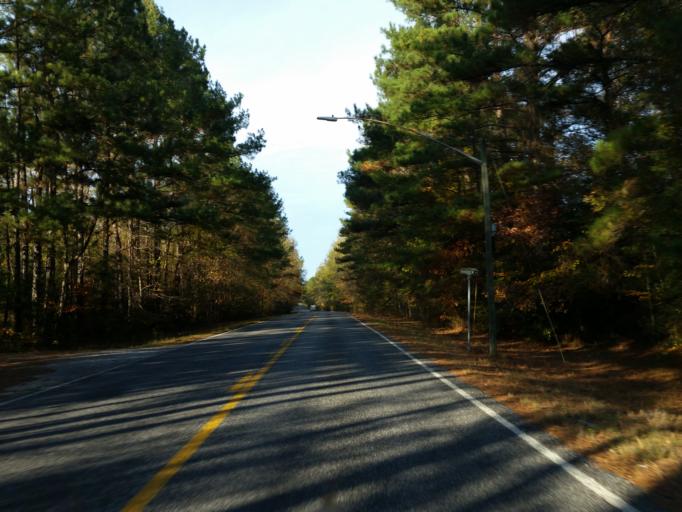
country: US
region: Mississippi
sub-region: Clarke County
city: Stonewall
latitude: 32.0504
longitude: -88.8820
